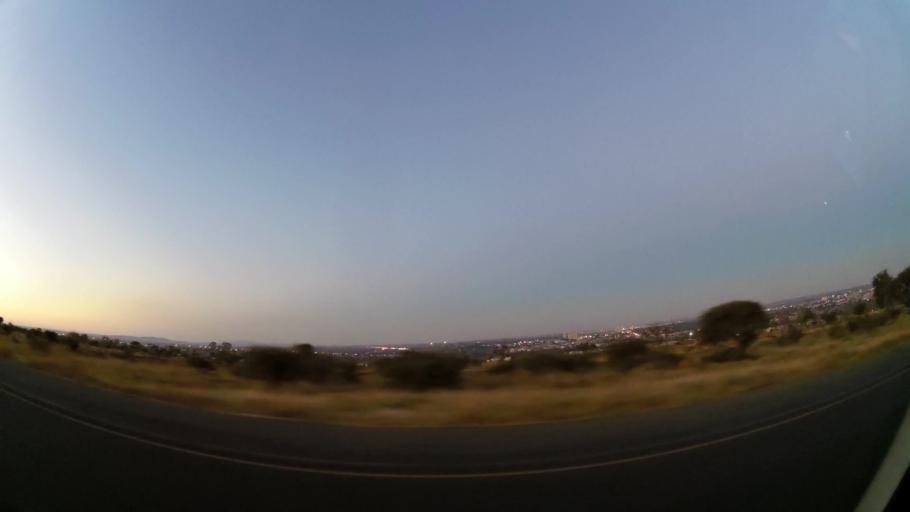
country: ZA
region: Limpopo
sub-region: Capricorn District Municipality
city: Polokwane
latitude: -23.8798
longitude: 29.4207
